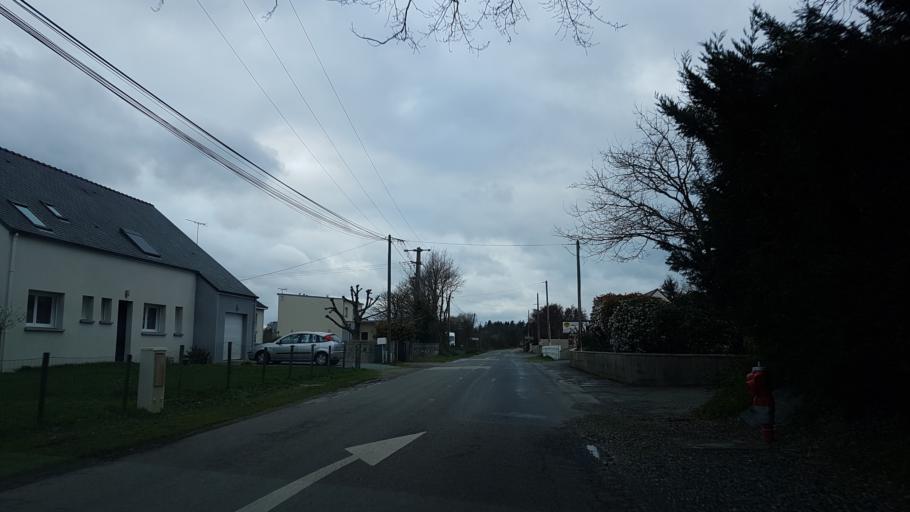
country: FR
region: Pays de la Loire
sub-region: Departement de la Loire-Atlantique
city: Le Gavre
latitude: 47.5245
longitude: -1.7562
